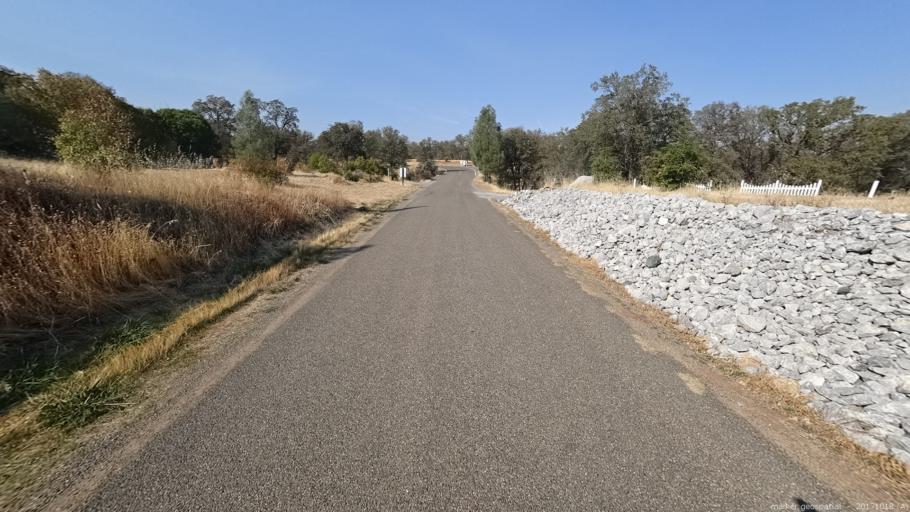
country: US
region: California
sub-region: Shasta County
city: Palo Cedro
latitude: 40.5594
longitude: -122.2569
